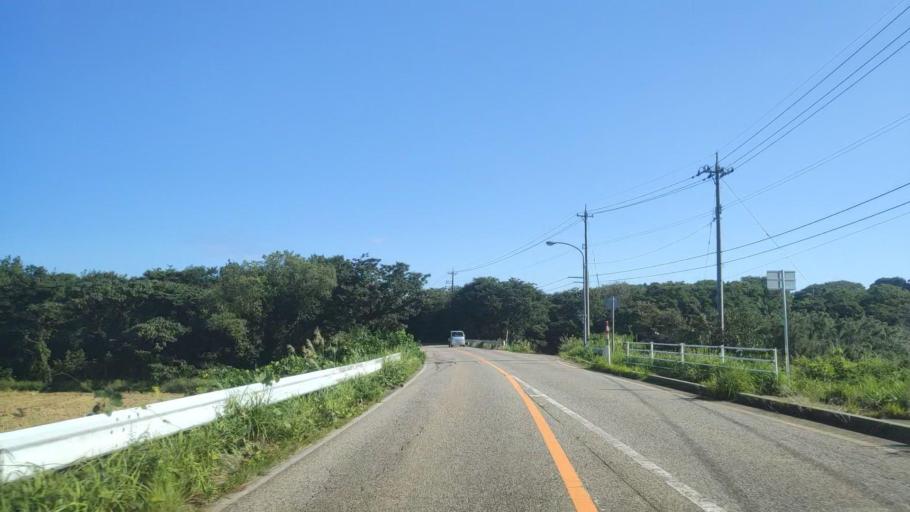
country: JP
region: Ishikawa
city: Hakui
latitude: 36.9603
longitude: 136.7730
